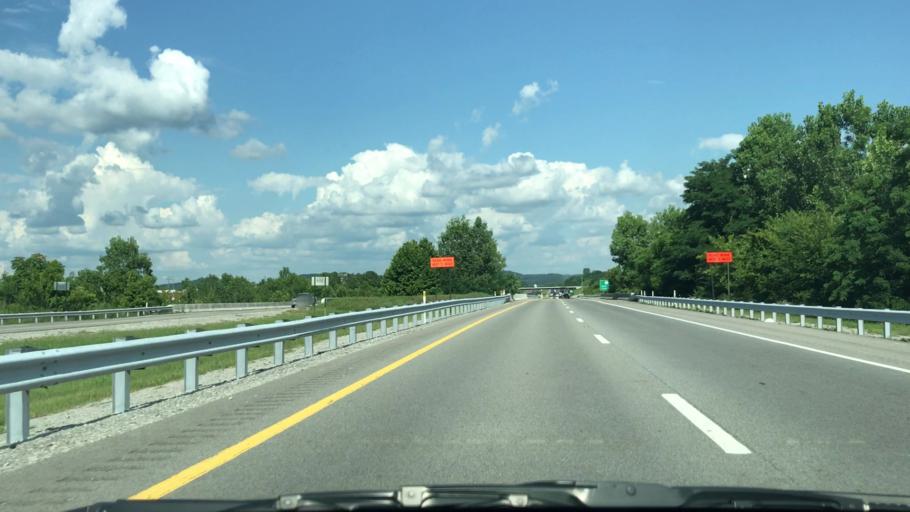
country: US
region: Tennessee
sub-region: Williamson County
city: Thompson's Station
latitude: 35.8227
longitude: -86.8992
